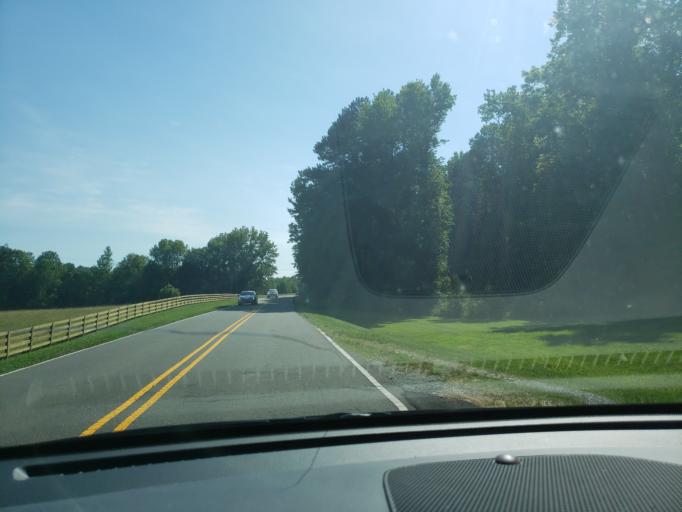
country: US
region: North Carolina
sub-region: Durham County
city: Gorman
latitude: 36.1231
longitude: -78.8953
